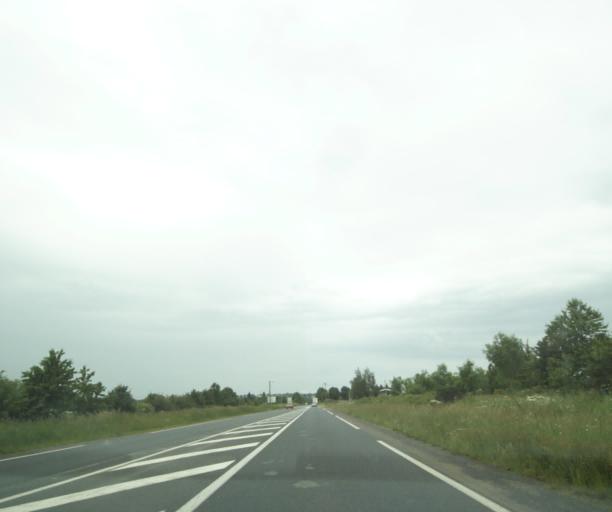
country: FR
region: Poitou-Charentes
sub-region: Departement des Deux-Sevres
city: Saint-Pardoux
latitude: 46.5498
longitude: -0.3110
